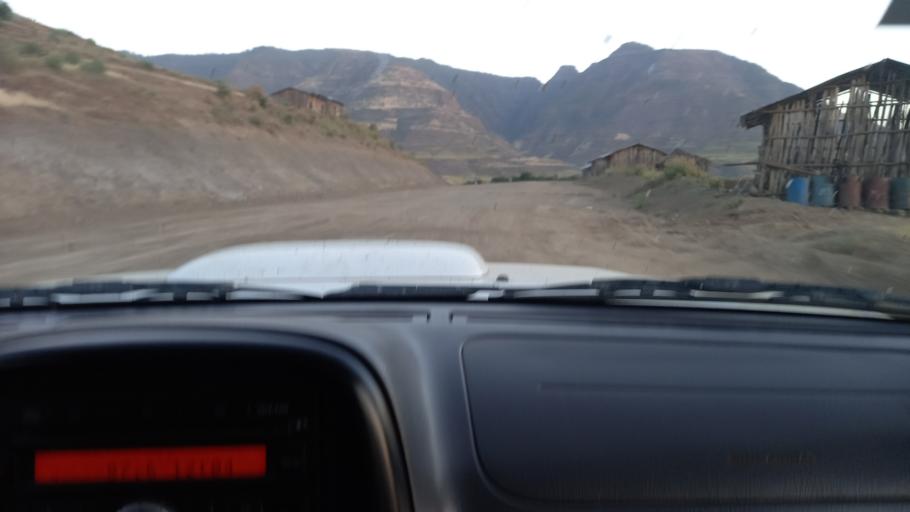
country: ET
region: Amhara
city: Debark'
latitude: 13.0374
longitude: 38.0406
